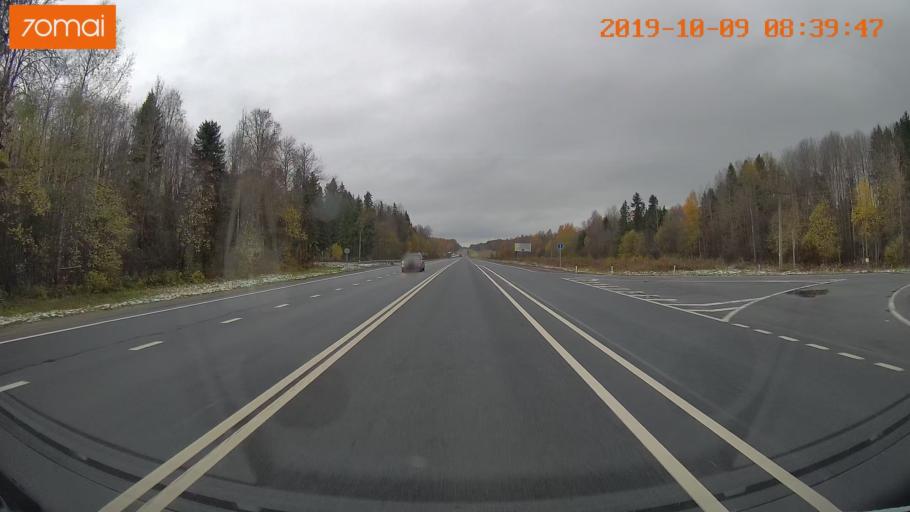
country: RU
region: Vologda
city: Gryazovets
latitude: 58.9767
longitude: 40.1487
